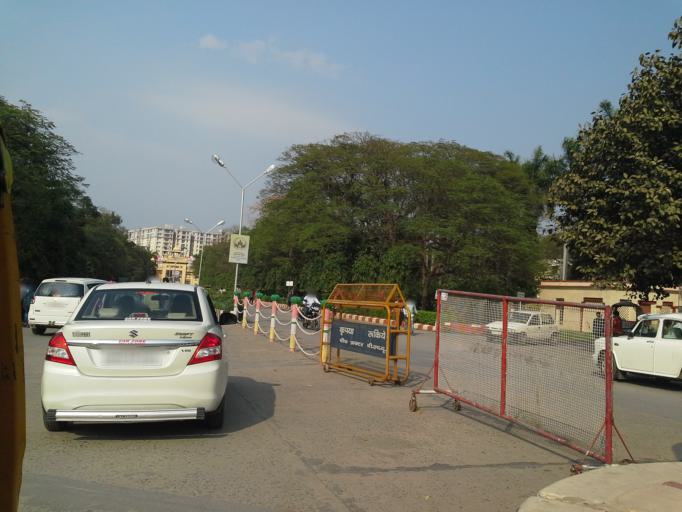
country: IN
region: Uttar Pradesh
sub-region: Varanasi
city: Ramnagar
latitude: 25.2755
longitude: 83.0008
